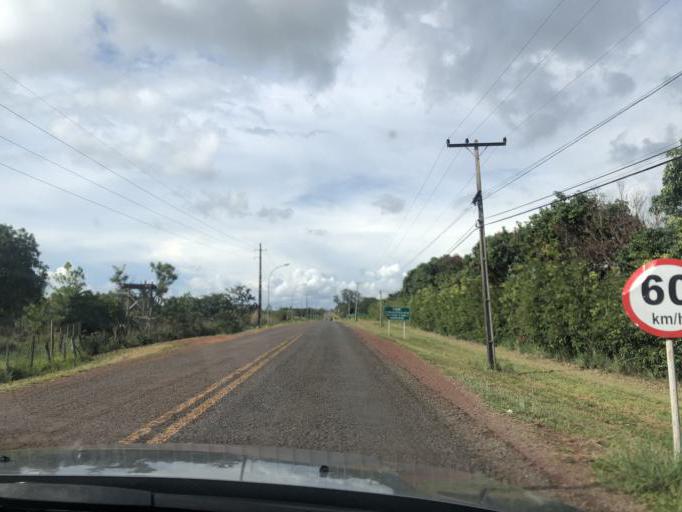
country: BR
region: Federal District
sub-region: Brasilia
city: Brasilia
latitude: -15.7464
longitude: -48.1259
